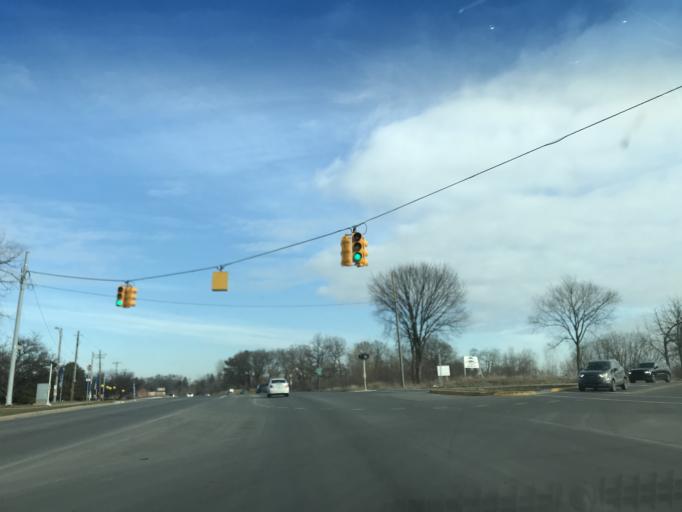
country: US
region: Michigan
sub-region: Oakland County
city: Auburn Hills
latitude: 42.6710
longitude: -83.2550
